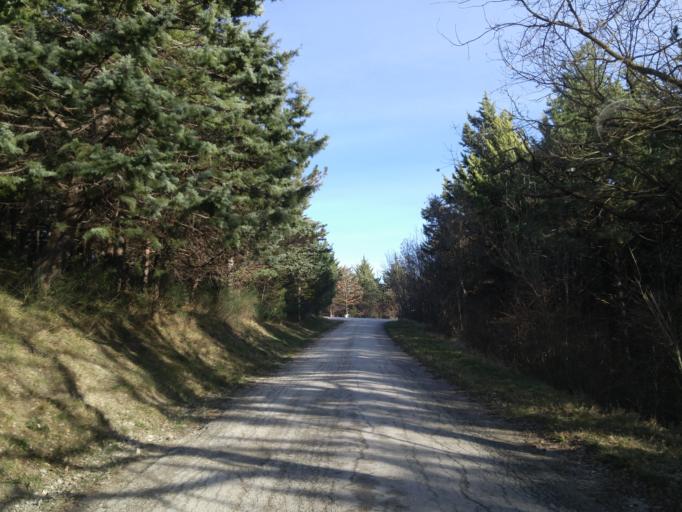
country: IT
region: The Marches
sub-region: Provincia di Pesaro e Urbino
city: Canavaccio
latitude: 43.6769
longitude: 12.6803
